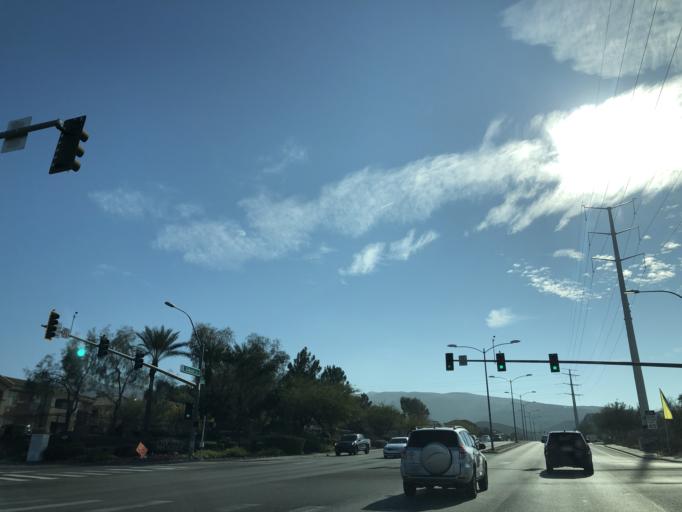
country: US
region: Nevada
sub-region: Clark County
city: Henderson
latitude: 36.0298
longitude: -115.0296
